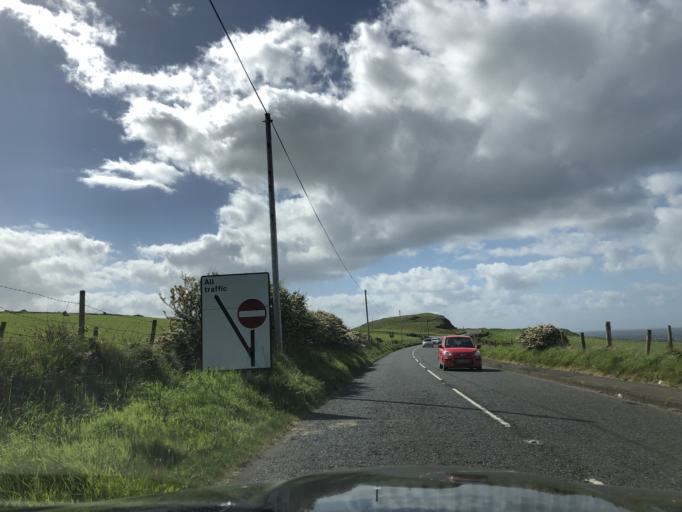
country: GB
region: Northern Ireland
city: Bushmills
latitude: 55.2120
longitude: -6.5692
